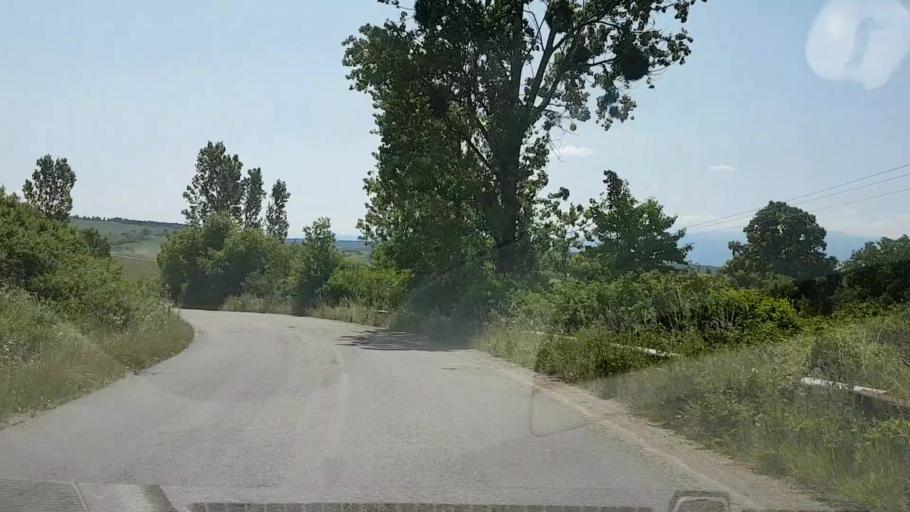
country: RO
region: Brasov
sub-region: Comuna Cincu
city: Cincu
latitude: 45.9340
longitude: 24.7905
